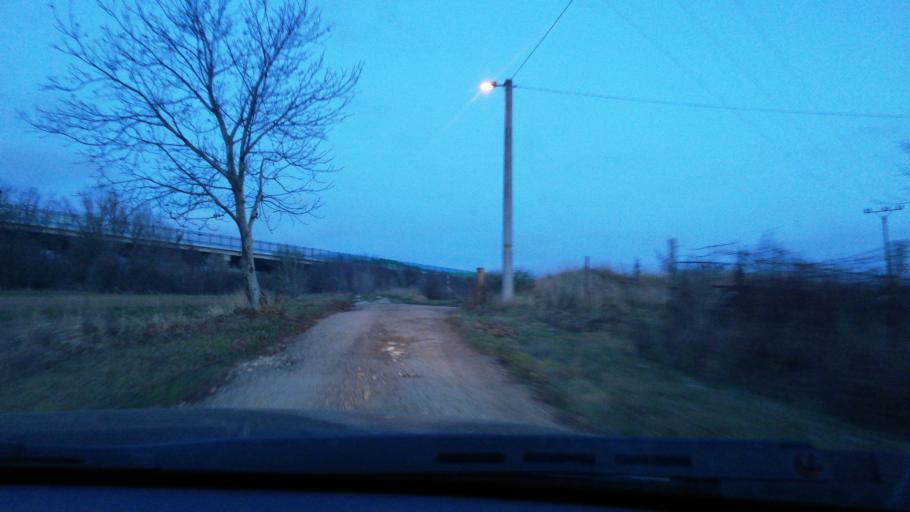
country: SK
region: Nitriansky
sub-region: Okres Nitra
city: Nitra
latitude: 48.3179
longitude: 17.9939
